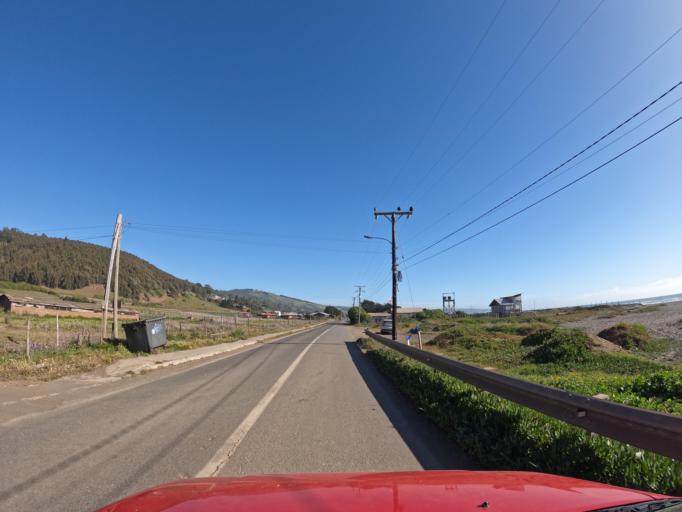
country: CL
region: Maule
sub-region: Provincia de Talca
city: Constitucion
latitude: -34.8364
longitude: -72.1429
